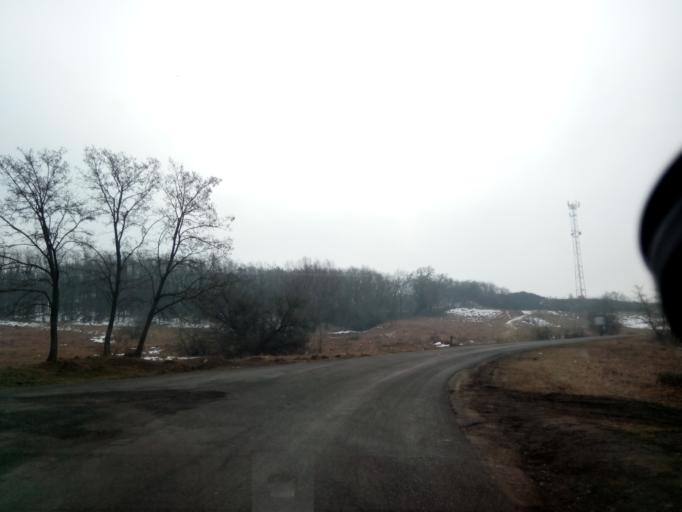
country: HU
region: Borsod-Abauj-Zemplen
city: Gonc
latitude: 48.4808
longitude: 21.2573
